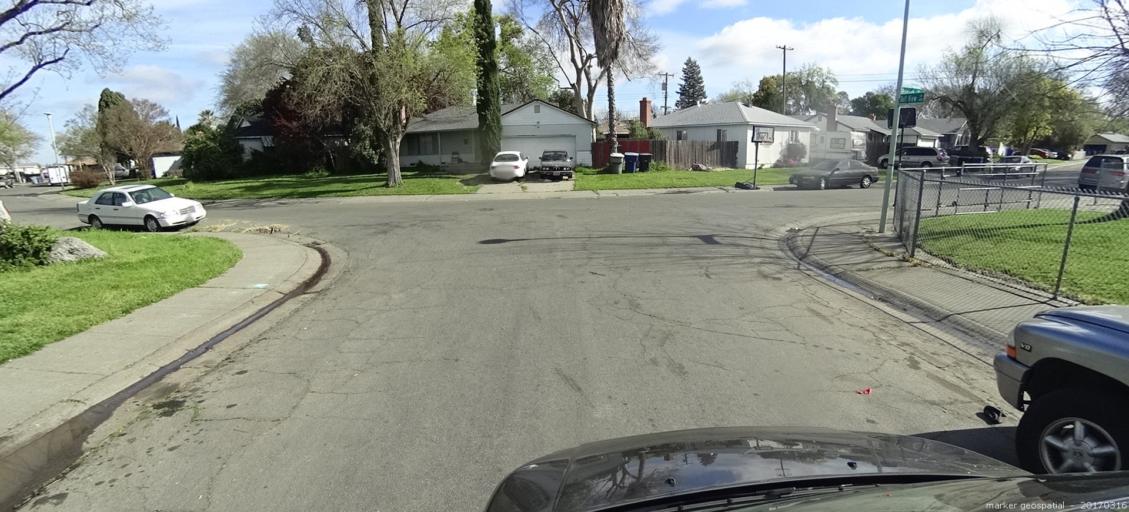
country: US
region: California
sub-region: Sacramento County
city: Parkway
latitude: 38.5104
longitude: -121.4917
